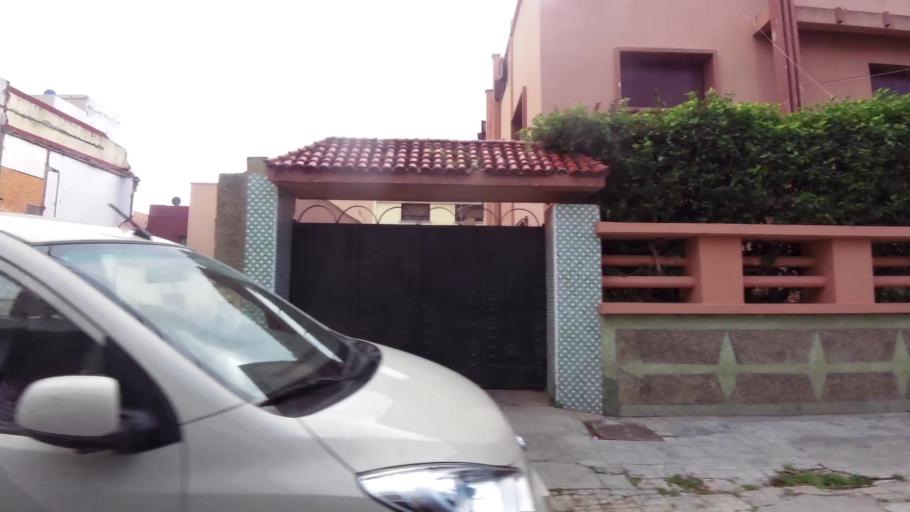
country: MA
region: Doukkala-Abda
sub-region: El-Jadida
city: El Jadida
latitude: 33.2451
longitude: -8.4965
